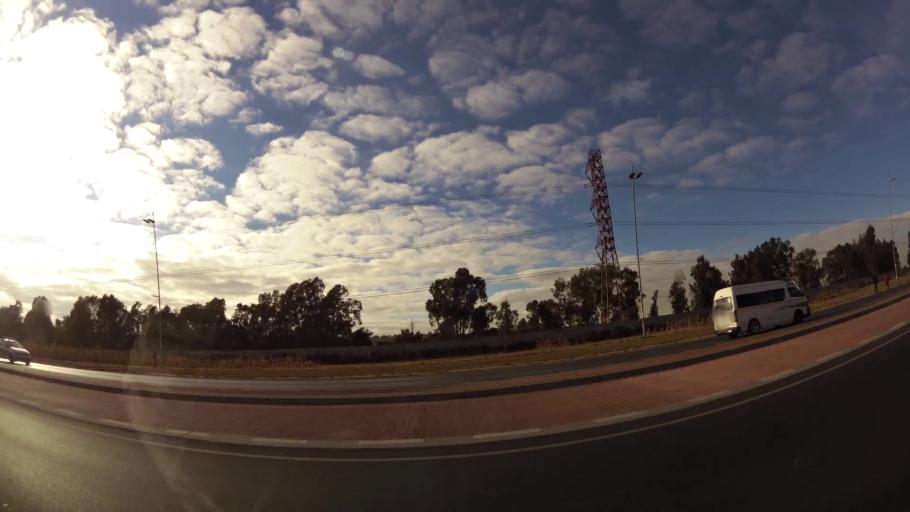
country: ZA
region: Gauteng
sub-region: City of Johannesburg Metropolitan Municipality
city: Modderfontein
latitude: -26.0445
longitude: 28.1878
